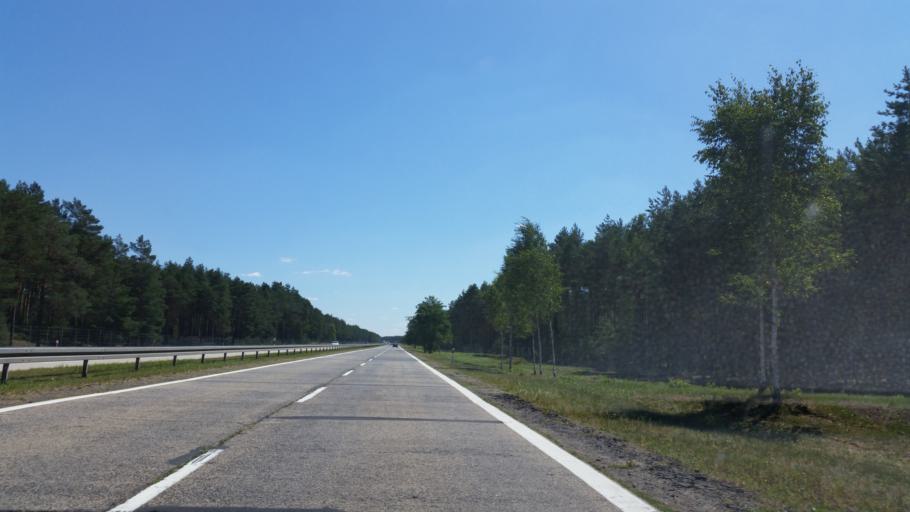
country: PL
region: Lubusz
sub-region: Powiat zaganski
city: Malomice
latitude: 51.4452
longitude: 15.3462
